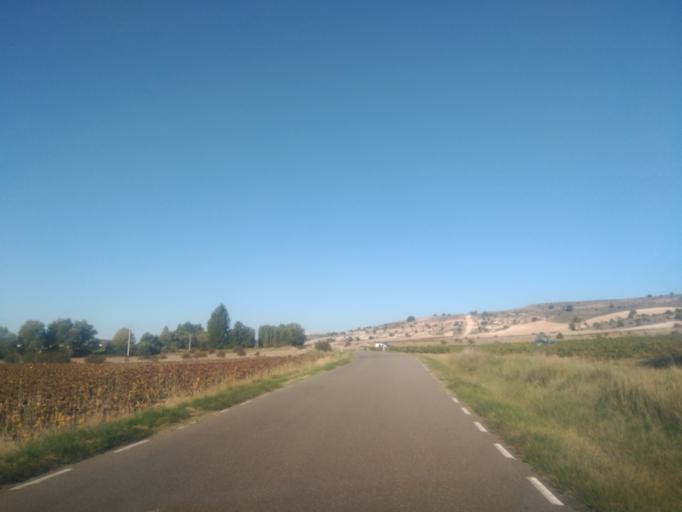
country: ES
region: Castille and Leon
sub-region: Provincia de Burgos
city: Penaranda de Duero
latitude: 41.6866
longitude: -3.4438
